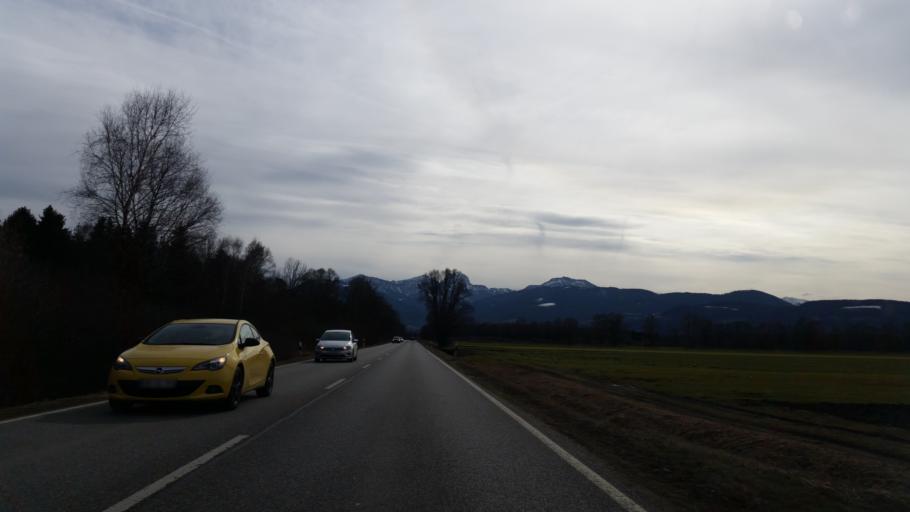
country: DE
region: Bavaria
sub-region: Upper Bavaria
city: Bad Aibling
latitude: 47.8357
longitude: 12.0119
